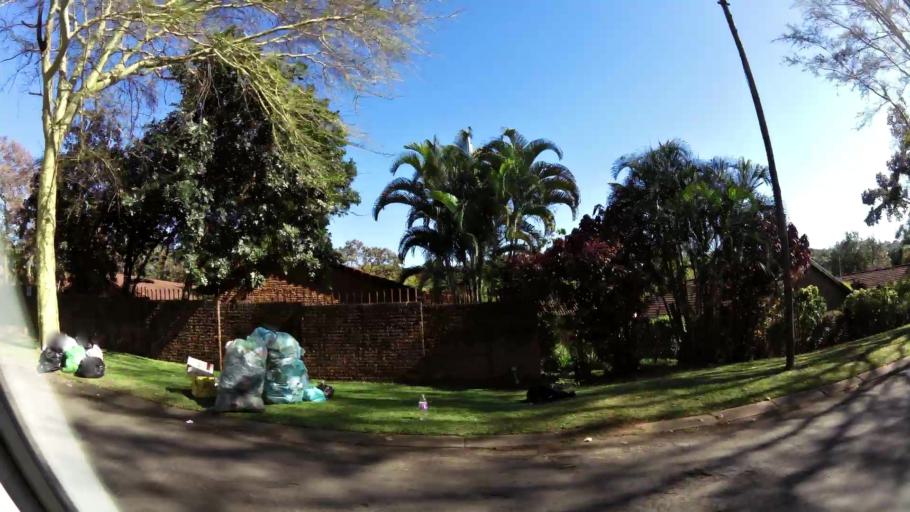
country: ZA
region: Limpopo
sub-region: Mopani District Municipality
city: Tzaneen
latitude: -23.8342
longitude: 30.1475
